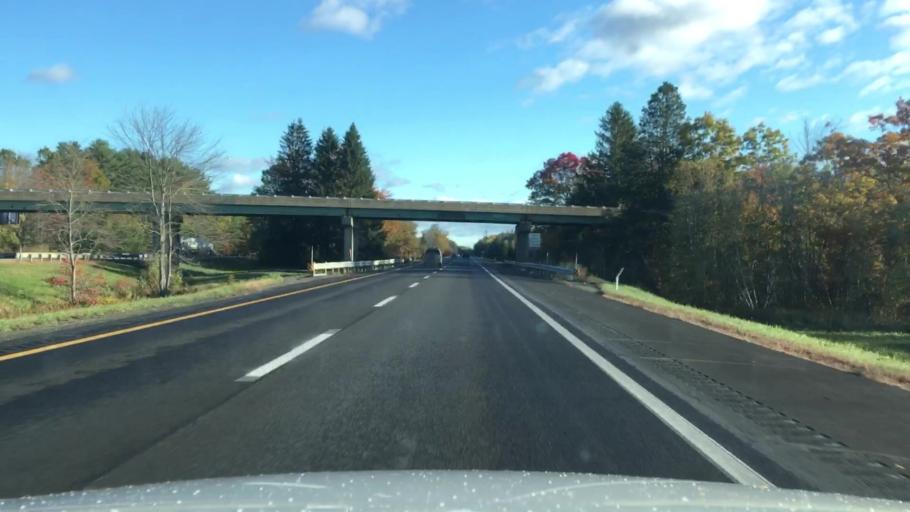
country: US
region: Maine
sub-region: Penobscot County
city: Veazie
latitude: 44.8453
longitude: -68.7309
